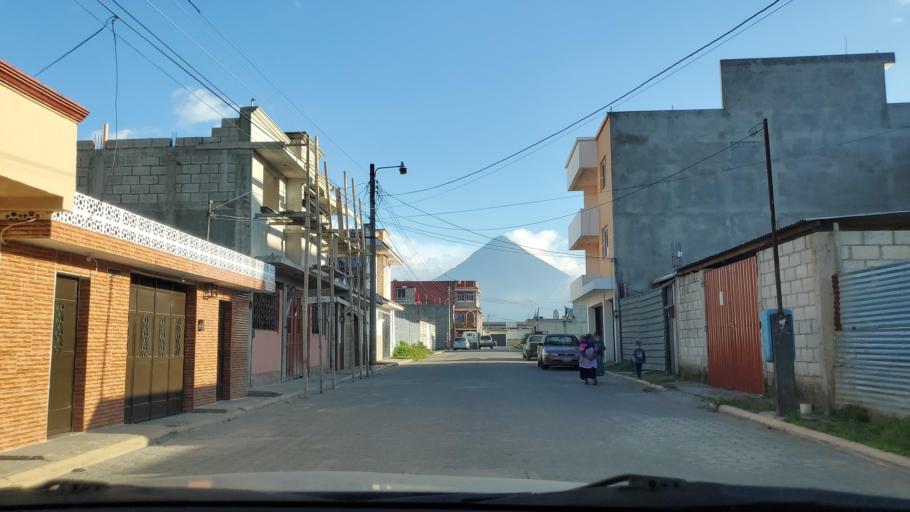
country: GT
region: Quetzaltenango
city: Quetzaltenango
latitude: 14.8360
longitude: -91.5457
